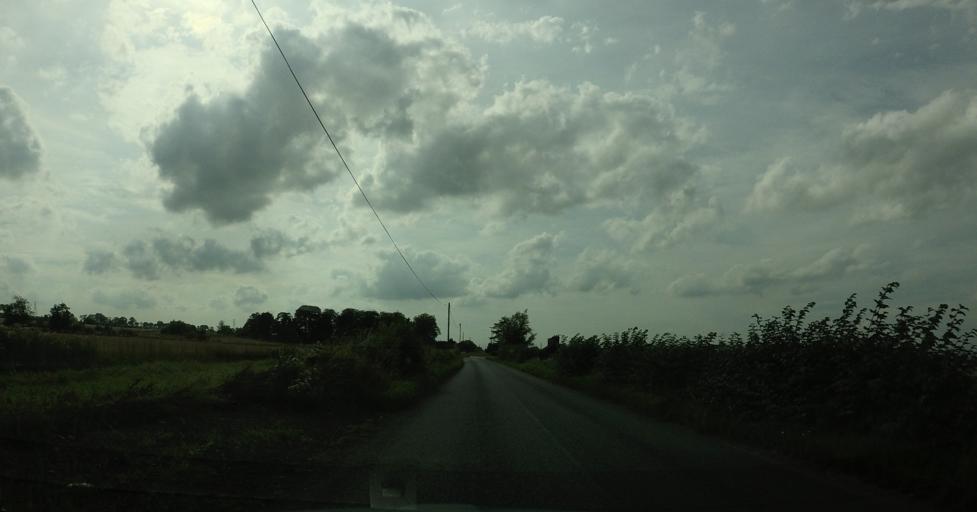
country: GB
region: Scotland
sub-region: Perth and Kinross
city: Methven
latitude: 56.3947
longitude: -3.5519
